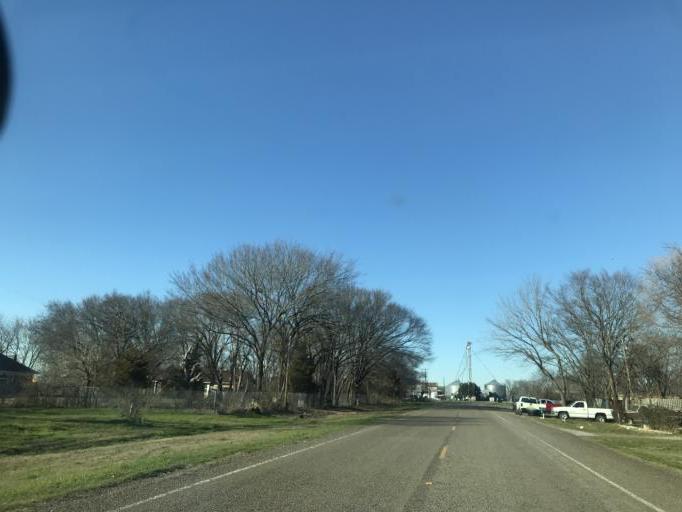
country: US
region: Texas
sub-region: Ellis County
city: Ferris
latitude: 32.4891
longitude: -96.6664
